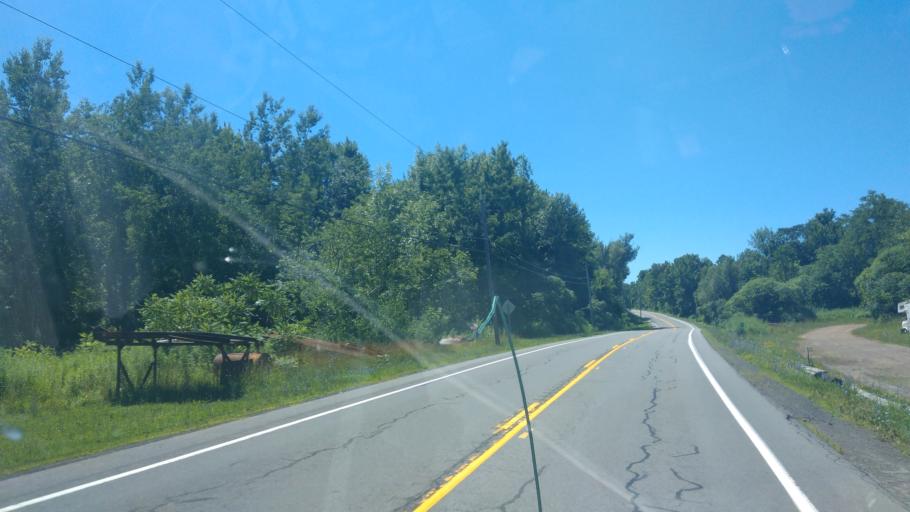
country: US
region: New York
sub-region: Wayne County
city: Sodus
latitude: 43.1750
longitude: -76.9876
